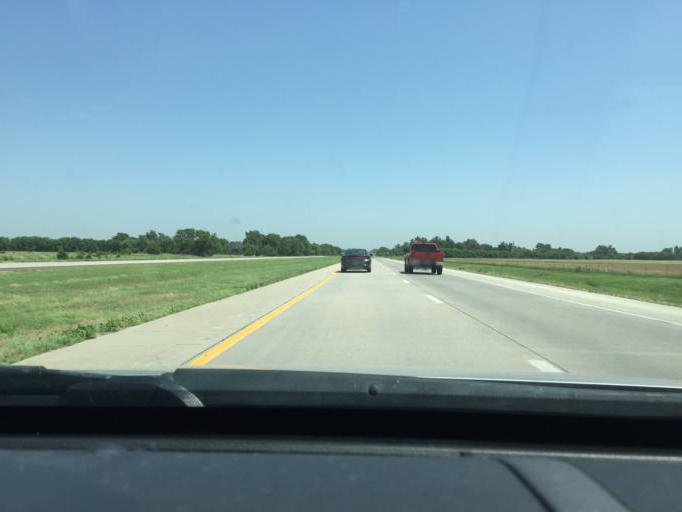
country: US
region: Kansas
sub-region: Reno County
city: Haven
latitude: 37.9316
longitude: -97.8537
